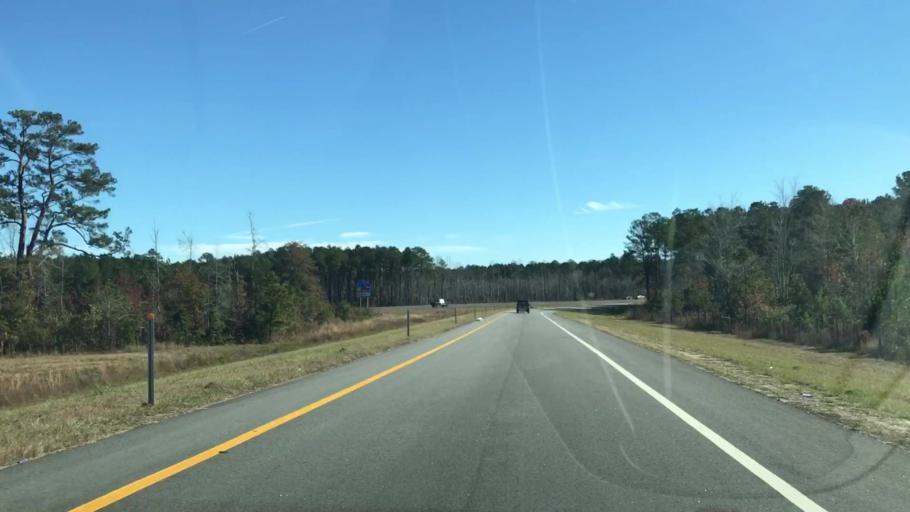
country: US
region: South Carolina
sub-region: Dorchester County
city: Summerville
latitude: 33.0517
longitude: -80.1650
